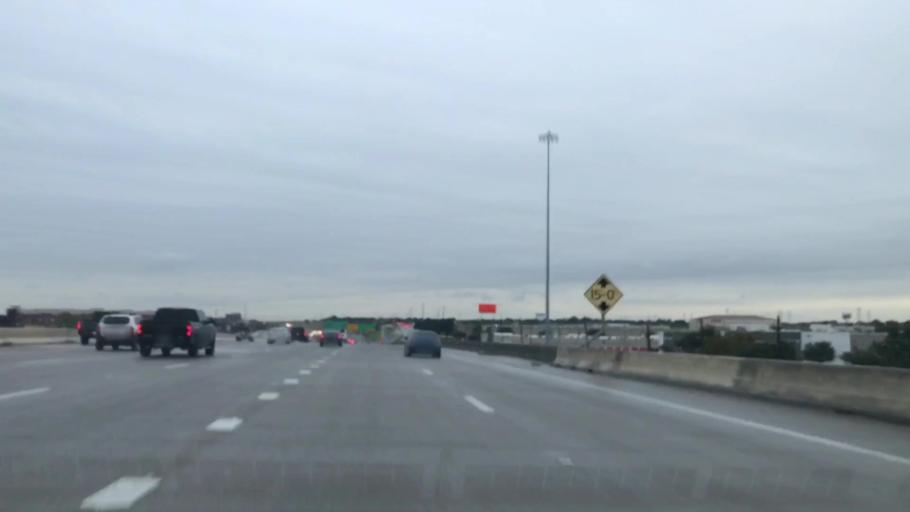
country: US
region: Texas
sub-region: Dallas County
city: Carrollton
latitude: 32.9831
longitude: -96.9202
